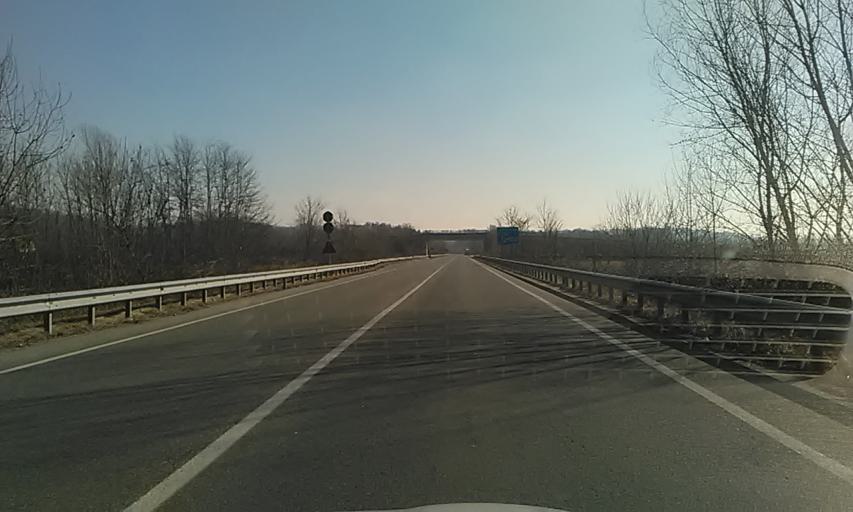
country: IT
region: Piedmont
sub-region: Provincia di Novara
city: Prato Sesia
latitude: 45.6658
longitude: 8.3637
